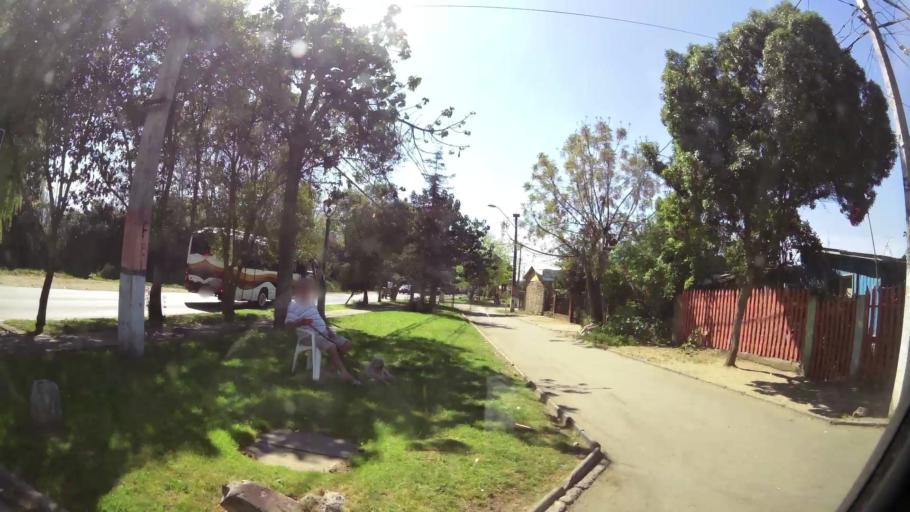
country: CL
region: Santiago Metropolitan
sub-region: Provincia de Talagante
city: Penaflor
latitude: -33.6119
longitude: -70.9054
